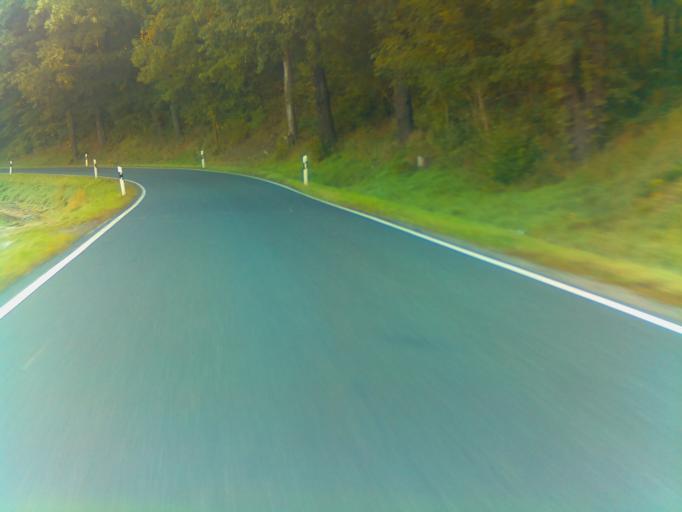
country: DE
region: Thuringia
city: Trobnitz
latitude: 50.8353
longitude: 11.7365
